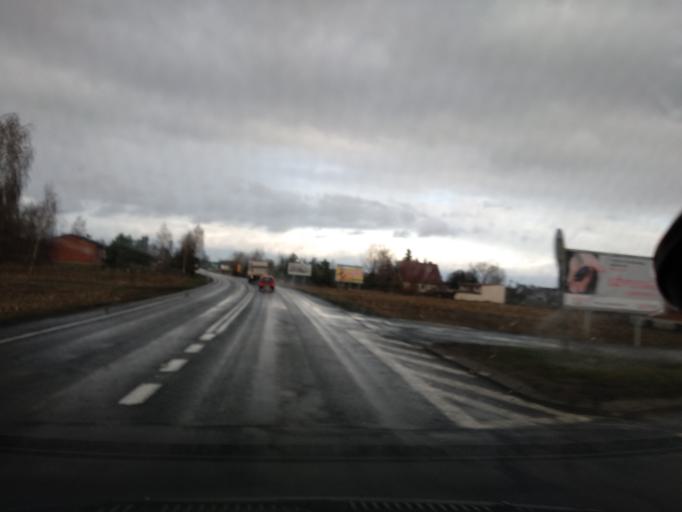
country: PL
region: Greater Poland Voivodeship
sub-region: Powiat koninski
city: Stare Miasto
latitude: 52.1544
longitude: 18.2055
